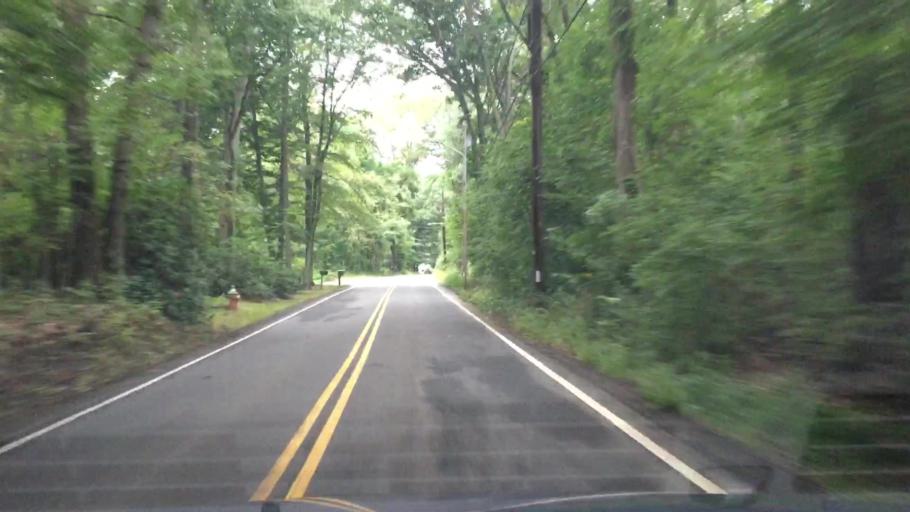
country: US
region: Massachusetts
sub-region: Essex County
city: North Andover
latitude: 42.7336
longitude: -71.1071
